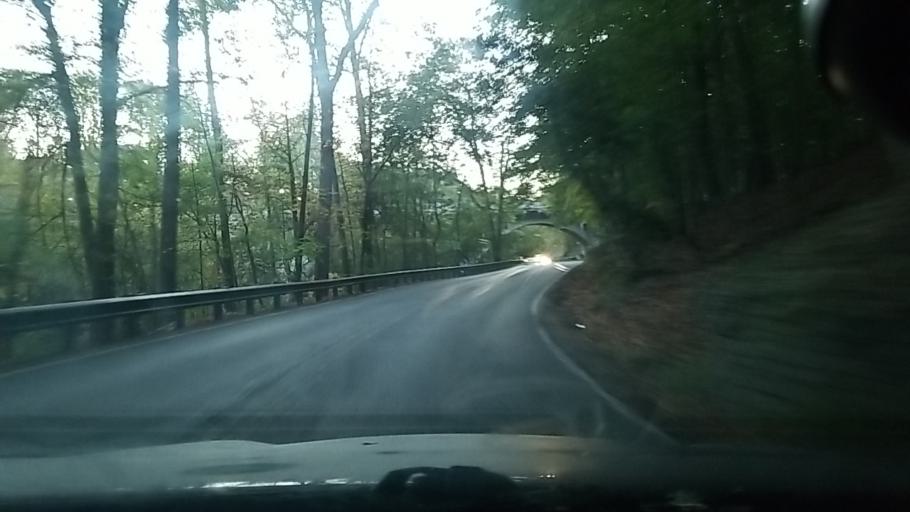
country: US
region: Maryland
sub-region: Montgomery County
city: Takoma Park
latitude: 38.9838
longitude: -77.0016
